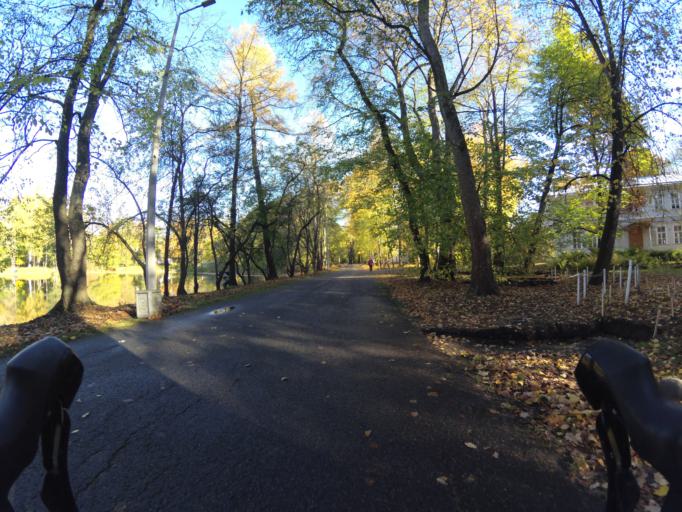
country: RU
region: Leningrad
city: Krestovskiy ostrov
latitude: 59.9804
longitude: 30.2618
